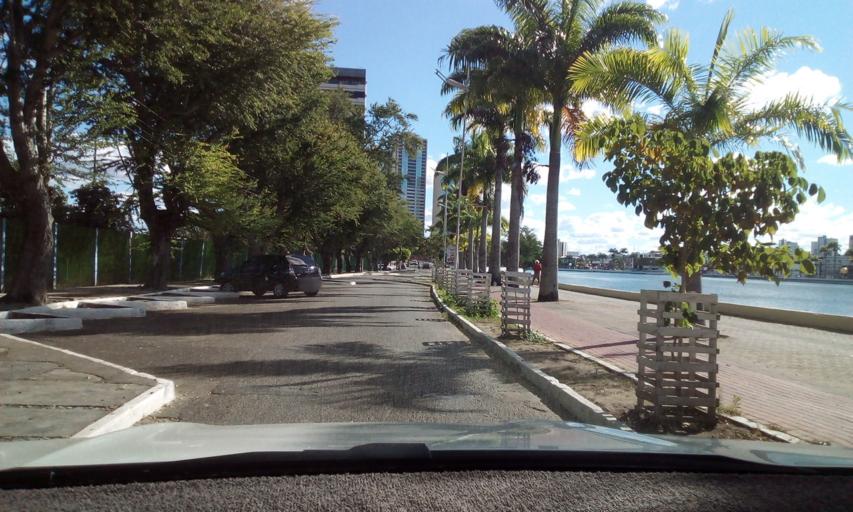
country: BR
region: Paraiba
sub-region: Campina Grande
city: Campina Grande
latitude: -7.2263
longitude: -35.8786
